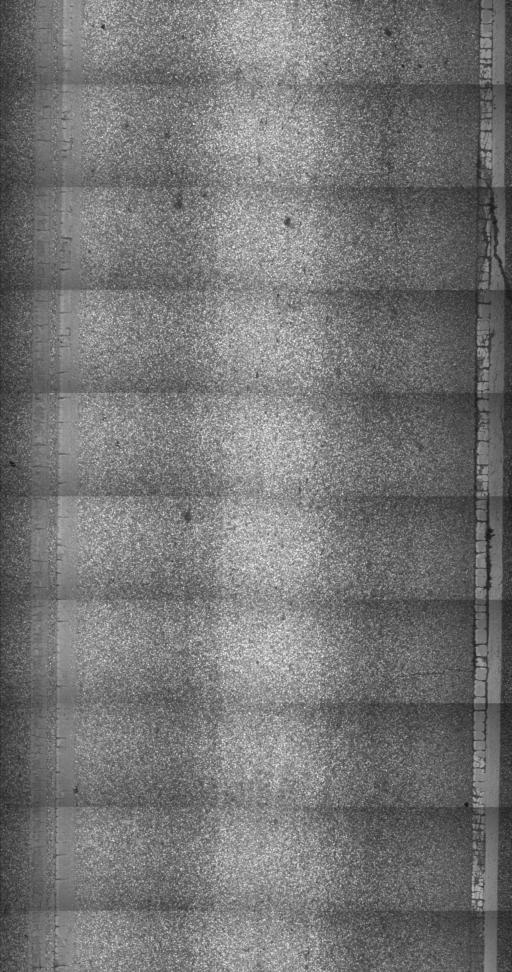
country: US
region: Vermont
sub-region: Rutland County
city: Fair Haven
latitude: 43.5835
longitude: -73.2649
